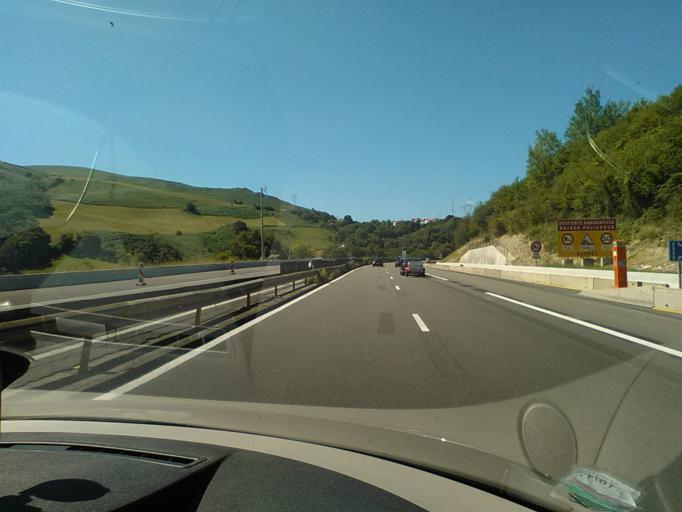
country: FR
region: Aquitaine
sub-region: Departement des Pyrenees-Atlantiques
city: Urrugne
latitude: 43.3461
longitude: -1.7217
